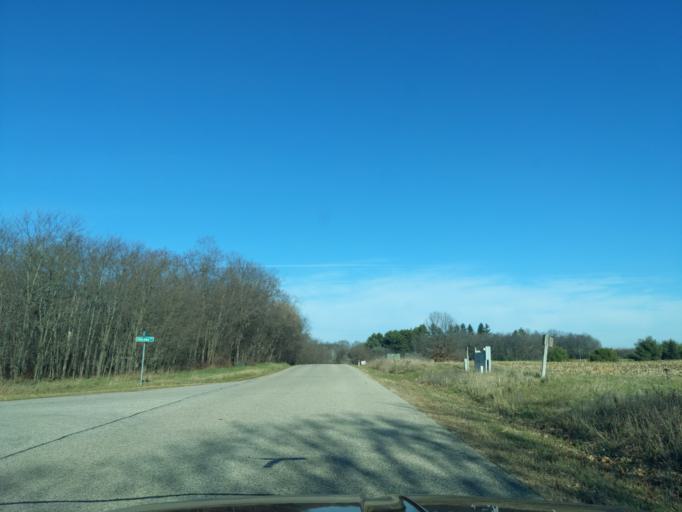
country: US
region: Wisconsin
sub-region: Waushara County
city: Silver Lake
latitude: 44.0679
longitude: -89.1937
